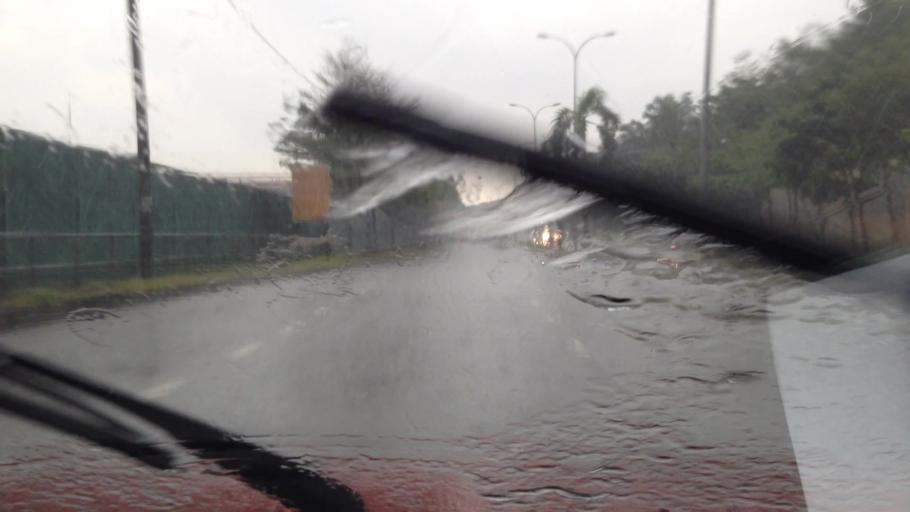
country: MY
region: Selangor
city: Subang Jaya
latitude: 3.0284
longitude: 101.5892
